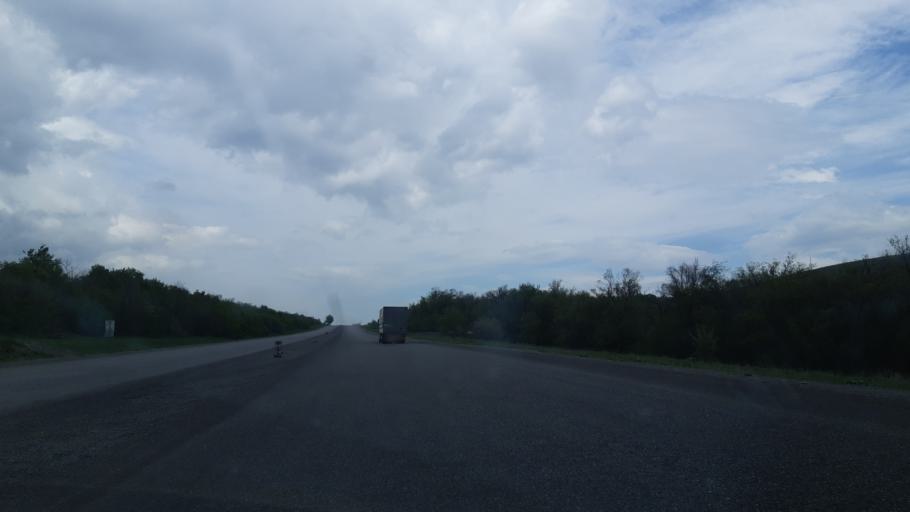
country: KZ
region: Ongtustik Qazaqstan
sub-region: Tulkibas Audany
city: Zhabagly
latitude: 42.5278
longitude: 70.5969
